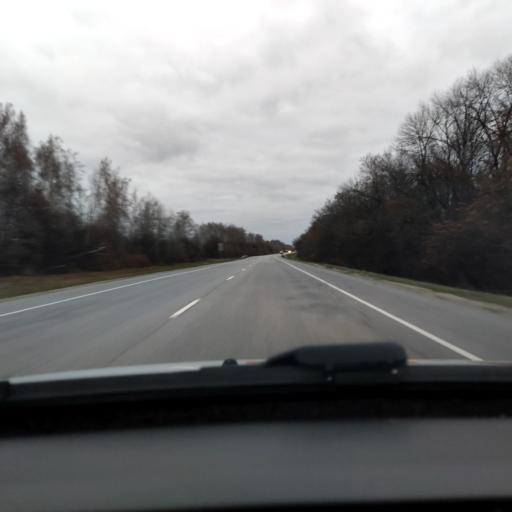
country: RU
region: Lipetsk
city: Borinskoye
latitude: 52.3676
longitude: 39.2064
